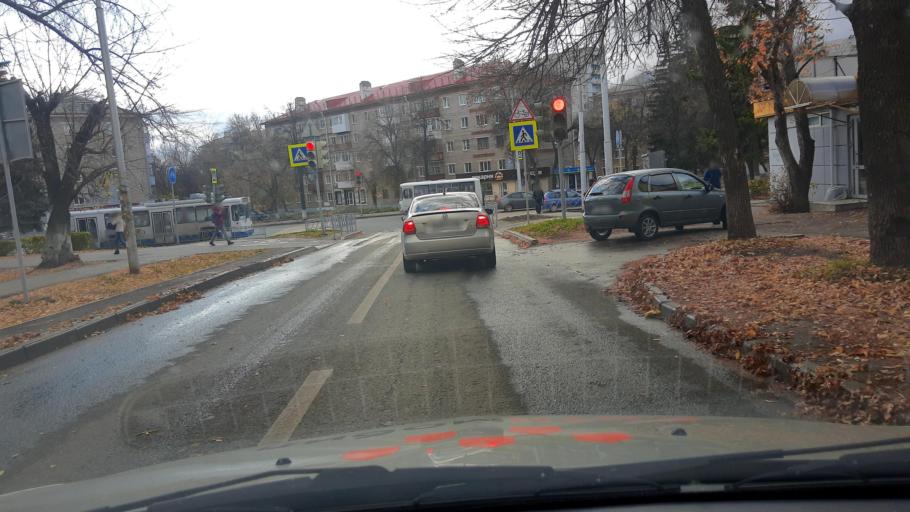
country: RU
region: Bashkortostan
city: Ufa
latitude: 54.8093
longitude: 56.1062
